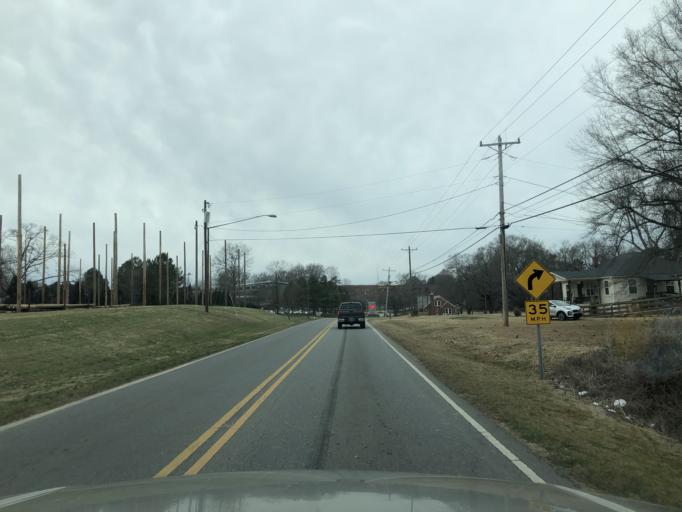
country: US
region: North Carolina
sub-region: Cleveland County
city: Shelby
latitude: 35.2765
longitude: -81.4864
